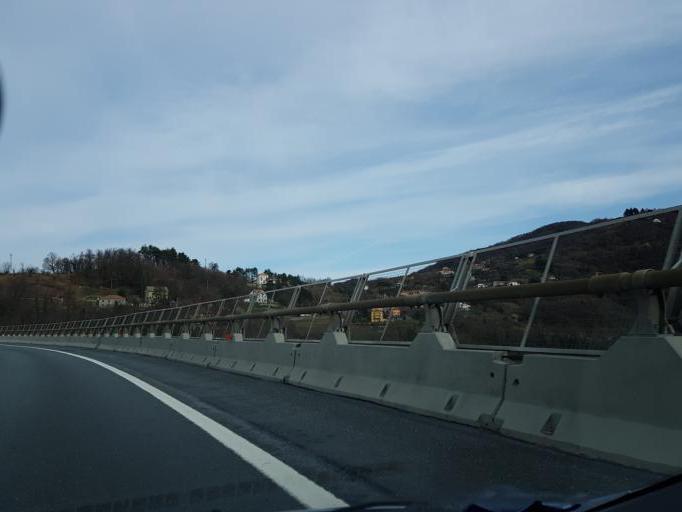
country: IT
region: Liguria
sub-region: Provincia di Genova
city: Serra Ricco
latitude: 44.5382
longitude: 8.9431
